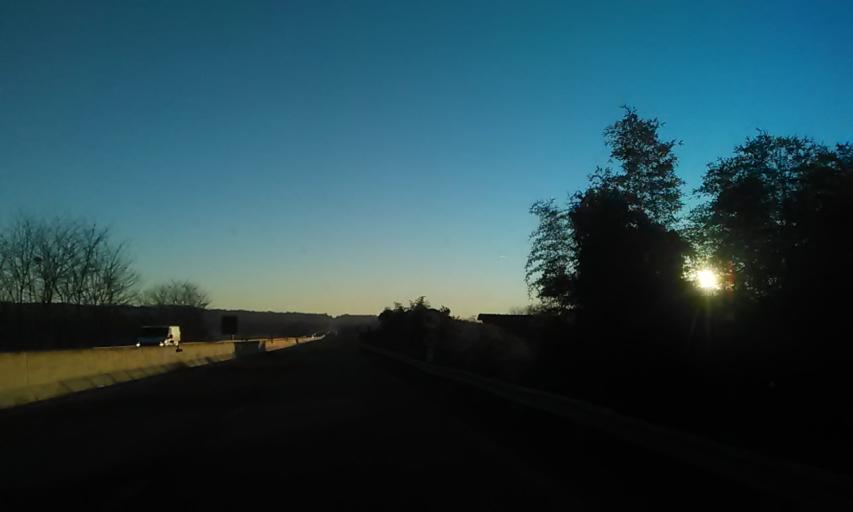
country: IT
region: Piedmont
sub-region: Provincia di Biella
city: Cerreto Castello
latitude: 45.5530
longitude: 8.1748
